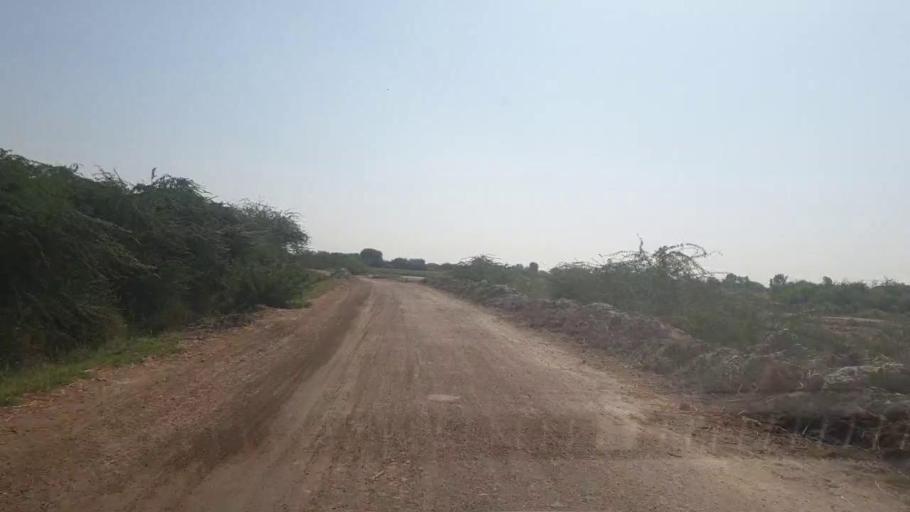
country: PK
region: Sindh
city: Badin
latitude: 24.5648
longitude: 68.8453
